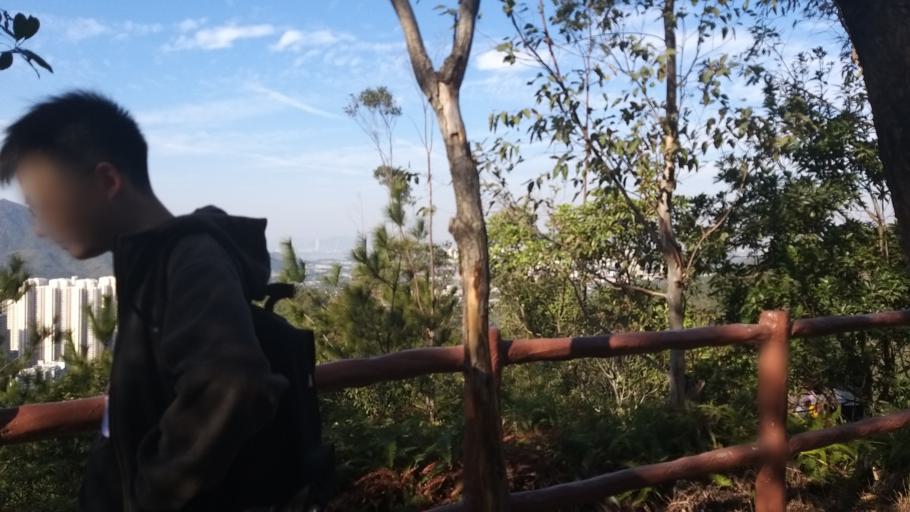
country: HK
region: Tuen Mun
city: Tuen Mun
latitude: 22.4044
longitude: 113.9884
